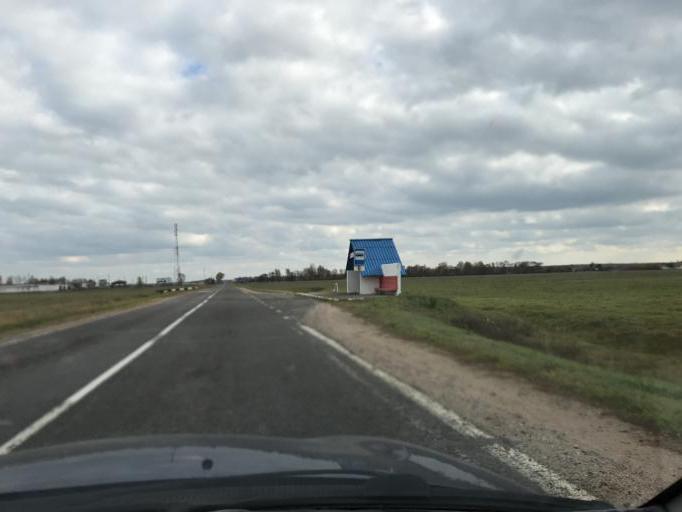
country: BY
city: Berezovka
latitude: 53.7407
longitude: 25.3619
